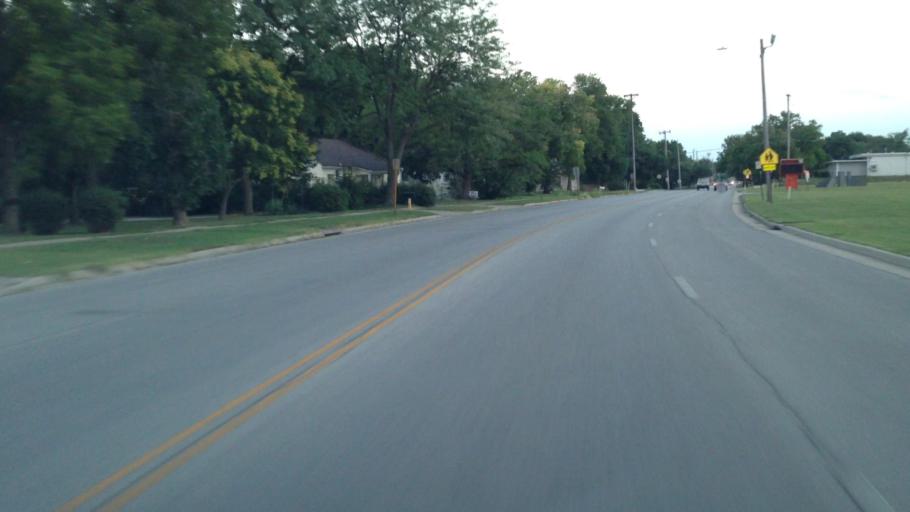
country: US
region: Kansas
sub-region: Montgomery County
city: Independence
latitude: 37.2379
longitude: -95.7108
